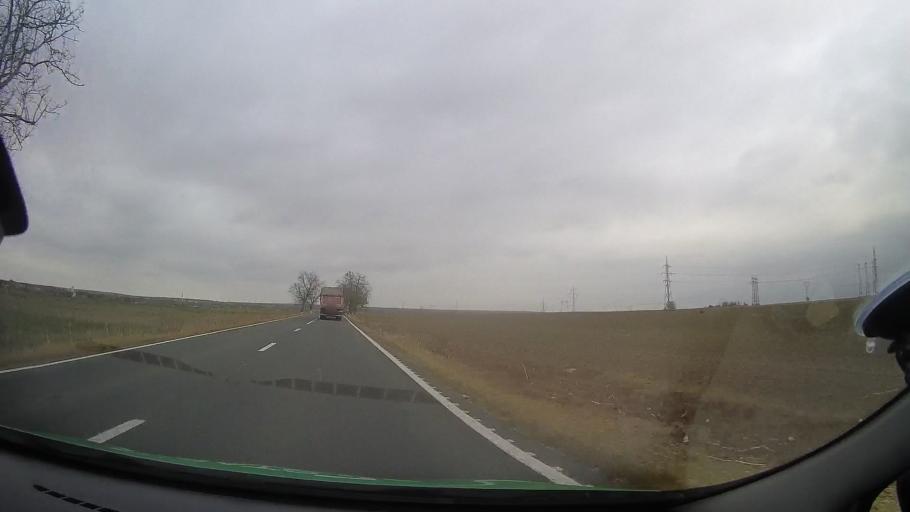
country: RO
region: Constanta
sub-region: Comuna Castelu
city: Castelu
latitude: 44.2556
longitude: 28.3513
